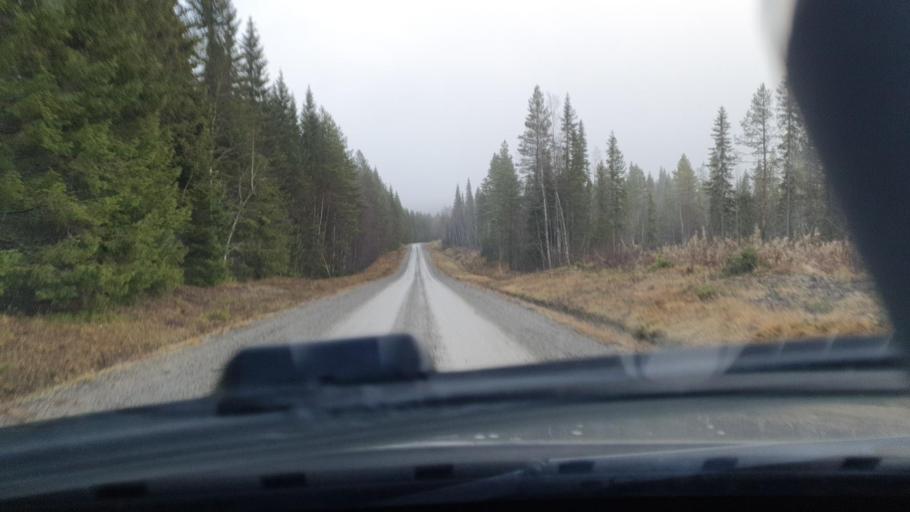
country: SE
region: Jaemtland
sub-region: Stroemsunds Kommun
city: Stroemsund
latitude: 63.5160
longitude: 15.6466
